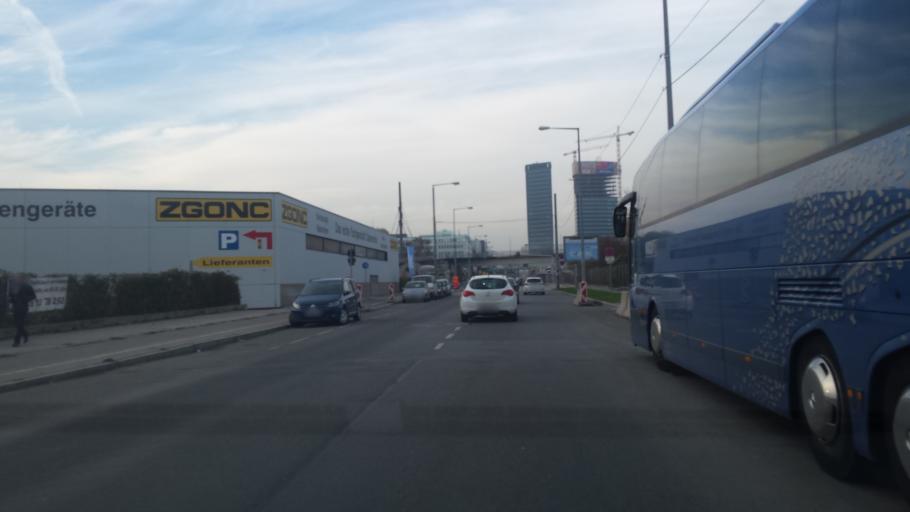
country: AT
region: Vienna
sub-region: Wien Stadt
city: Vienna
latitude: 48.1877
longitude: 16.4197
